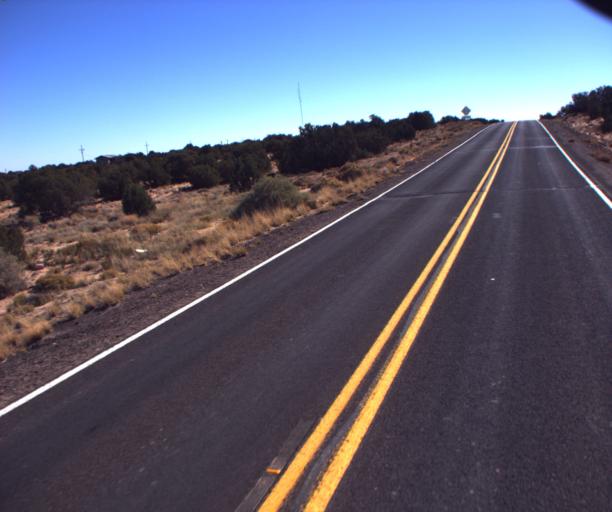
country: US
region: Arizona
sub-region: Navajo County
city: First Mesa
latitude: 35.8476
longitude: -110.5342
